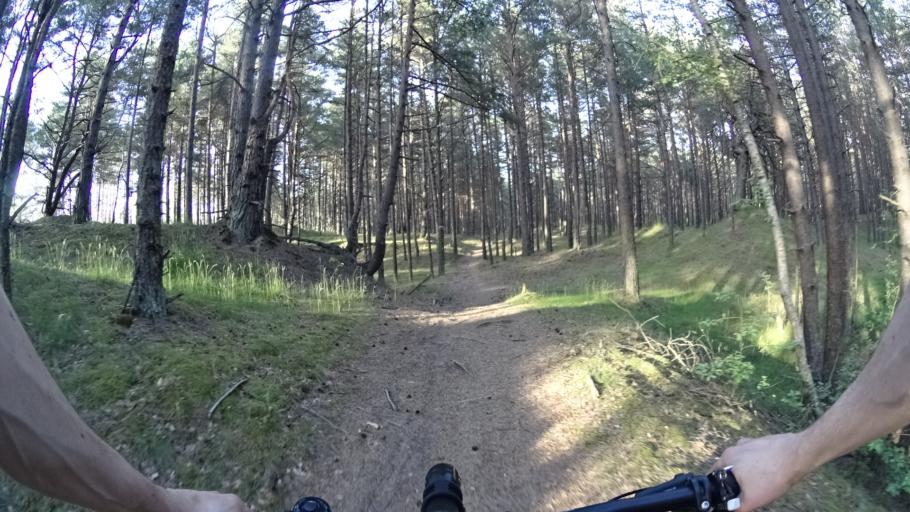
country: LV
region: Riga
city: Jaunciems
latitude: 57.0980
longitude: 24.1558
